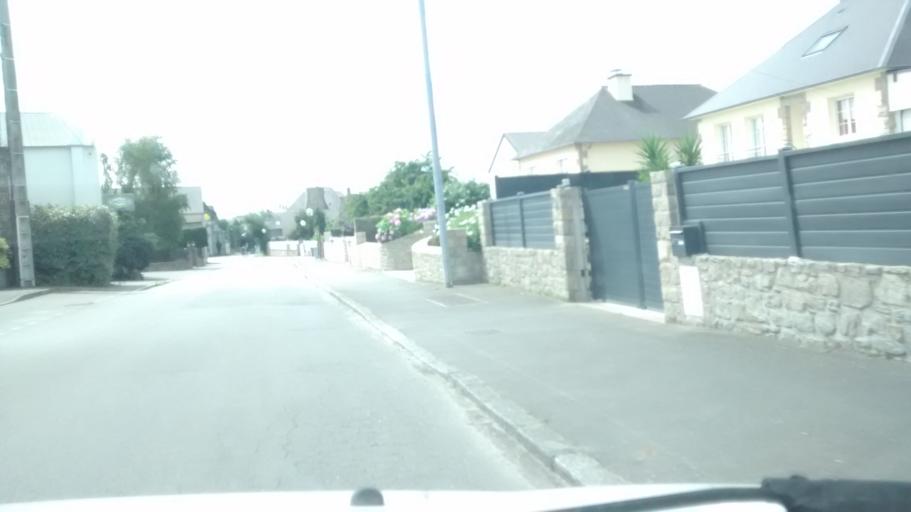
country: FR
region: Brittany
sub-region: Departement d'Ille-et-Vilaine
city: La Gouesniere
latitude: 48.6058
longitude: -1.8953
